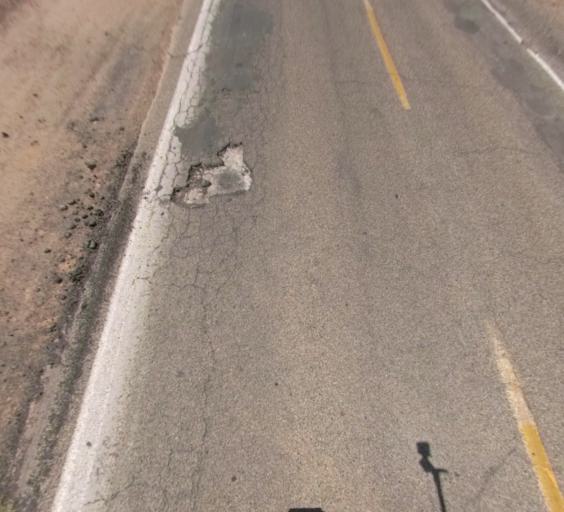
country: US
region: California
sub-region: Madera County
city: Madera Acres
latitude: 36.9967
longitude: -120.0286
